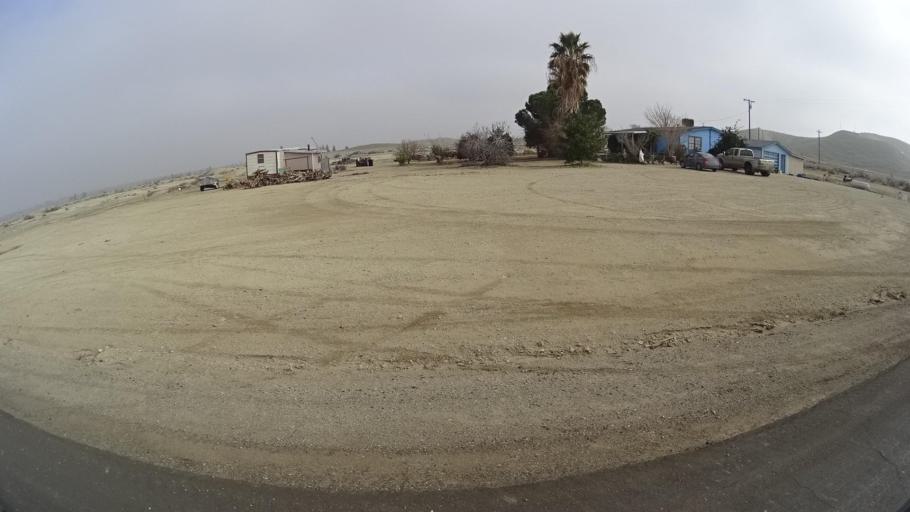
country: US
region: California
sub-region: Kern County
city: Maricopa
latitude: 35.0384
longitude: -119.3670
